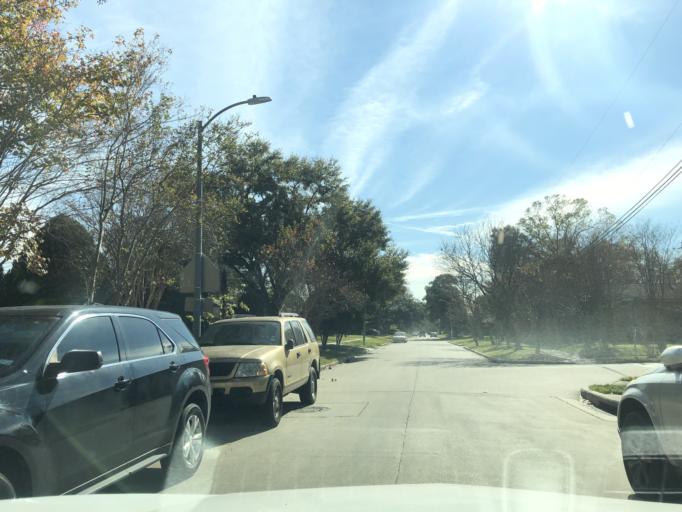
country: US
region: Texas
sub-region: Harris County
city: Bellaire
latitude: 29.6847
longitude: -95.5059
